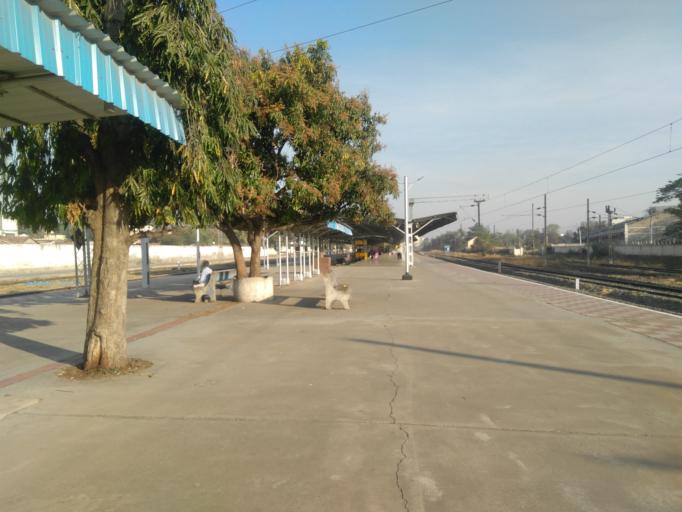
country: IN
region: Tamil Nadu
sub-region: Coimbatore
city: Coimbatore
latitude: 11.0186
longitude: 76.9553
